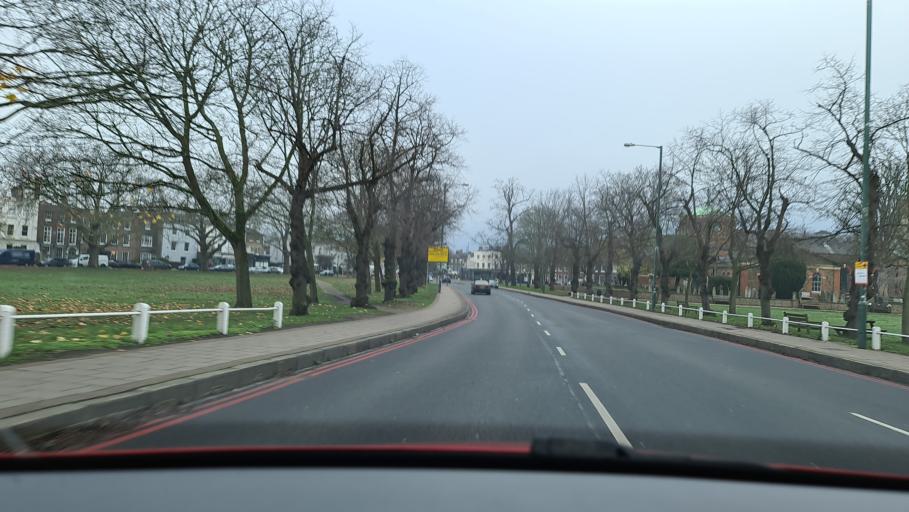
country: GB
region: England
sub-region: Greater London
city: Brentford
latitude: 51.4849
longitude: -0.2874
